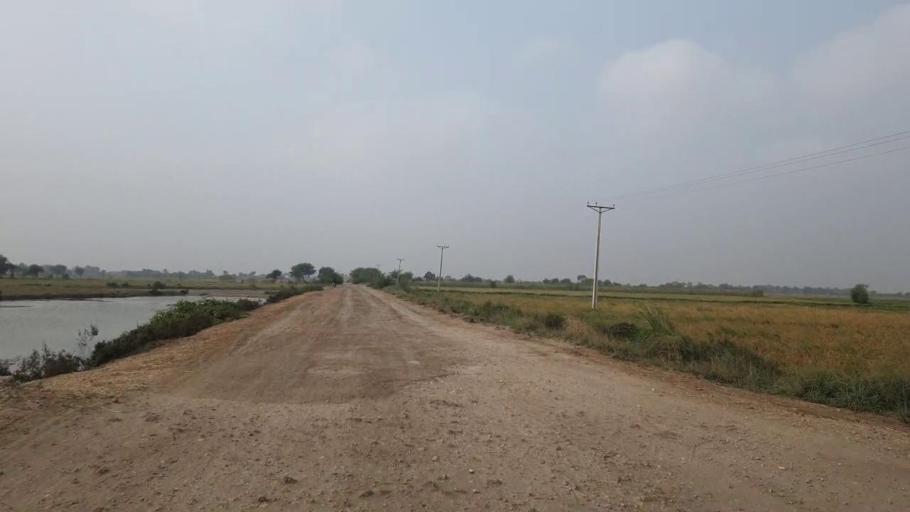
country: PK
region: Sindh
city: Matli
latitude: 24.9749
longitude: 68.6107
